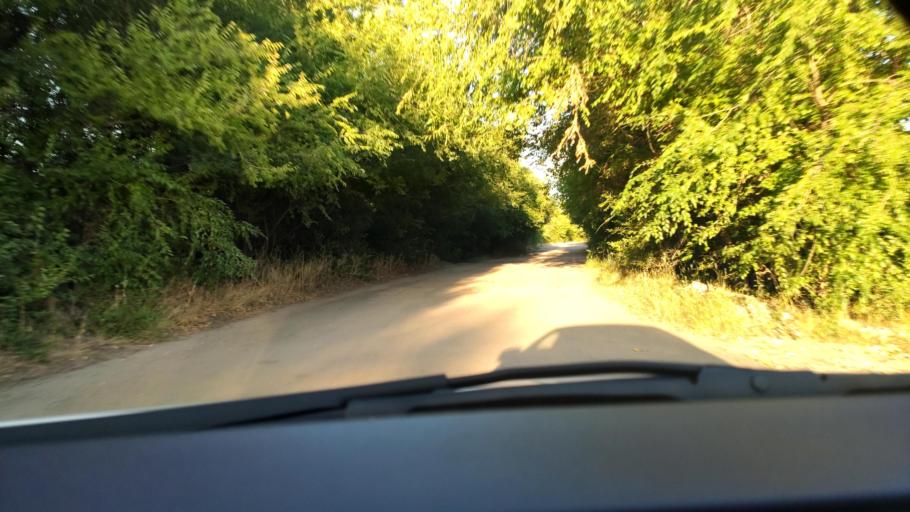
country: RU
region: Voronezj
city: Pridonskoy
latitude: 51.6847
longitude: 39.0604
